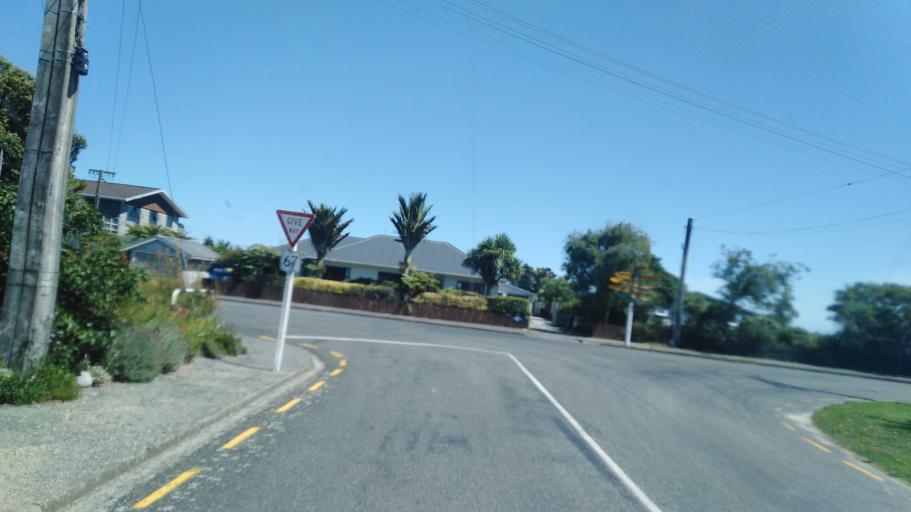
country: NZ
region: West Coast
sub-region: Buller District
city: Westport
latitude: -41.2477
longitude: 172.1118
